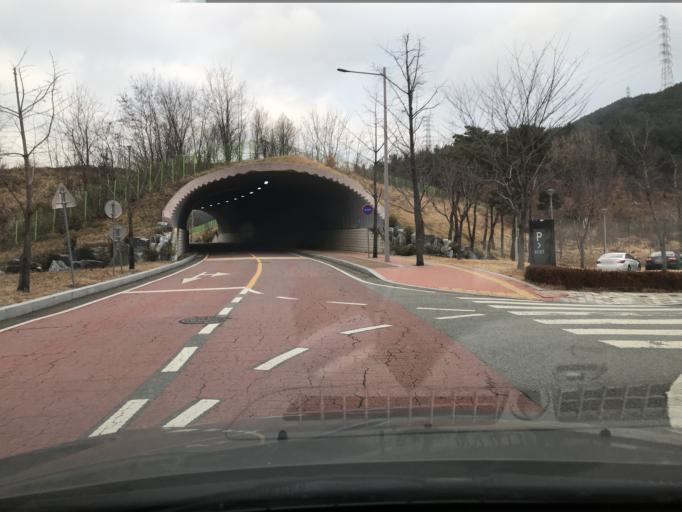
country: KR
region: Daegu
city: Hwawon
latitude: 35.7040
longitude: 128.4611
